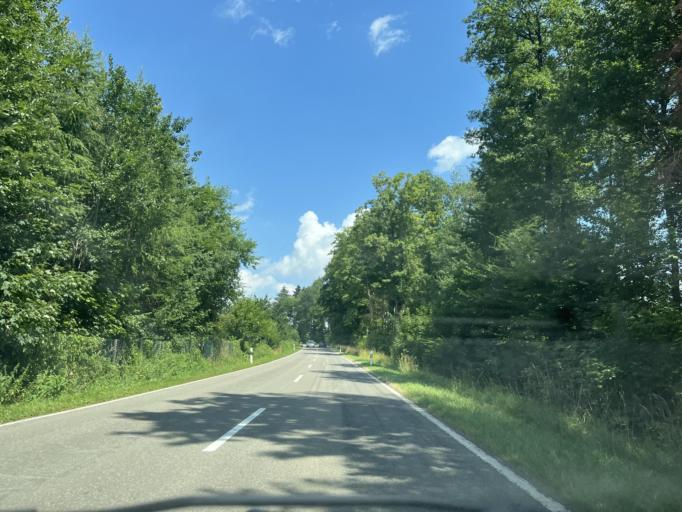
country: DE
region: Baden-Wuerttemberg
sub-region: Tuebingen Region
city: Wald
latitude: 47.9519
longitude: 9.1736
